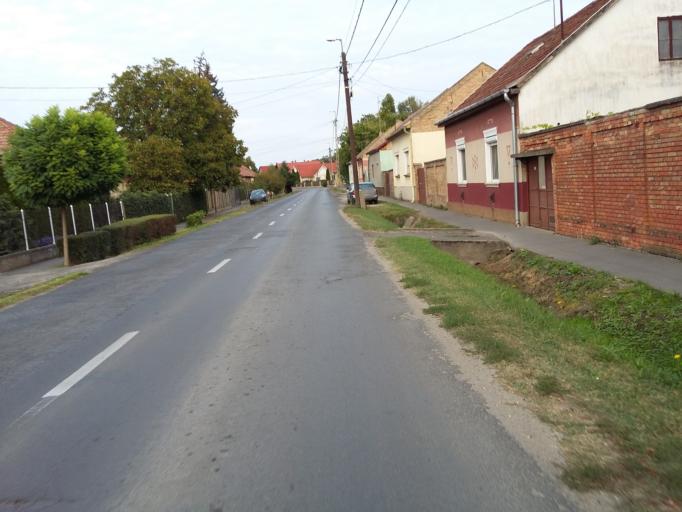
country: HU
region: Csongrad
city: Szeged
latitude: 46.2302
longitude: 20.1157
